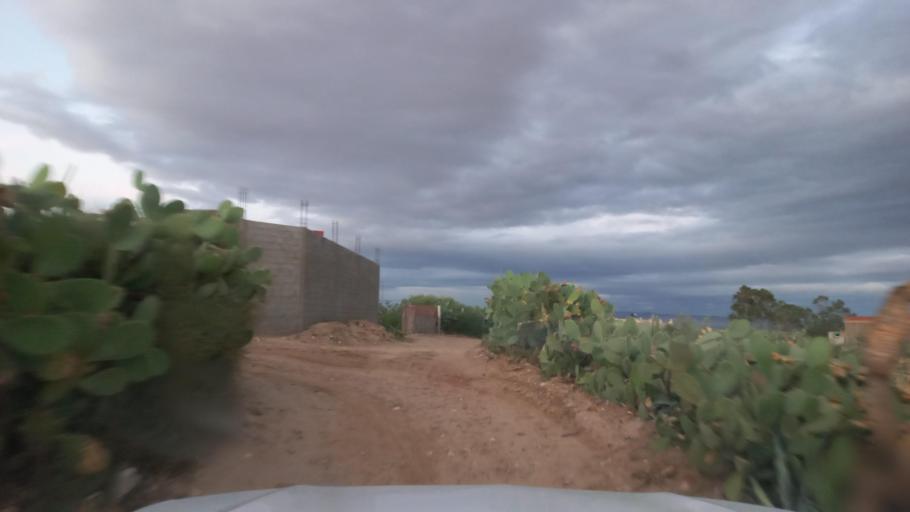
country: TN
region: Al Qasrayn
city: Kasserine
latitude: 35.2570
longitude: 8.9381
